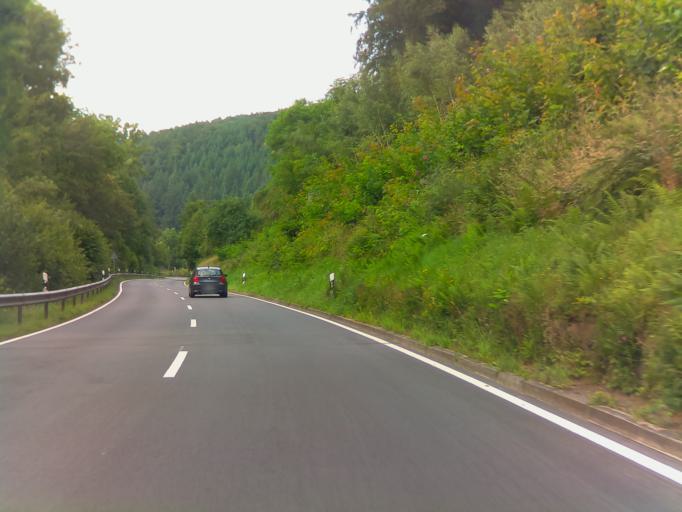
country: DE
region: Baden-Wuerttemberg
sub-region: Karlsruhe Region
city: Schonau
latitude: 49.4251
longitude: 8.8099
